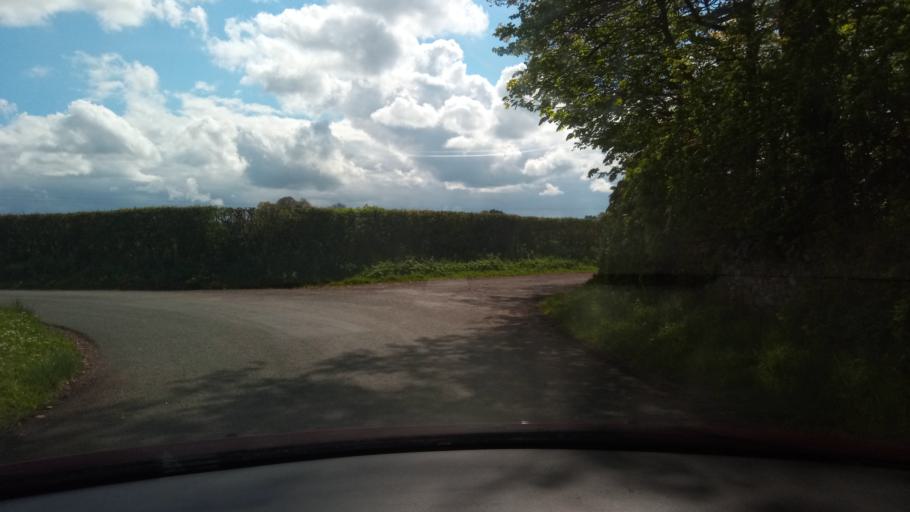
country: GB
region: Scotland
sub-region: The Scottish Borders
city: Saint Boswells
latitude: 55.5621
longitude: -2.6180
